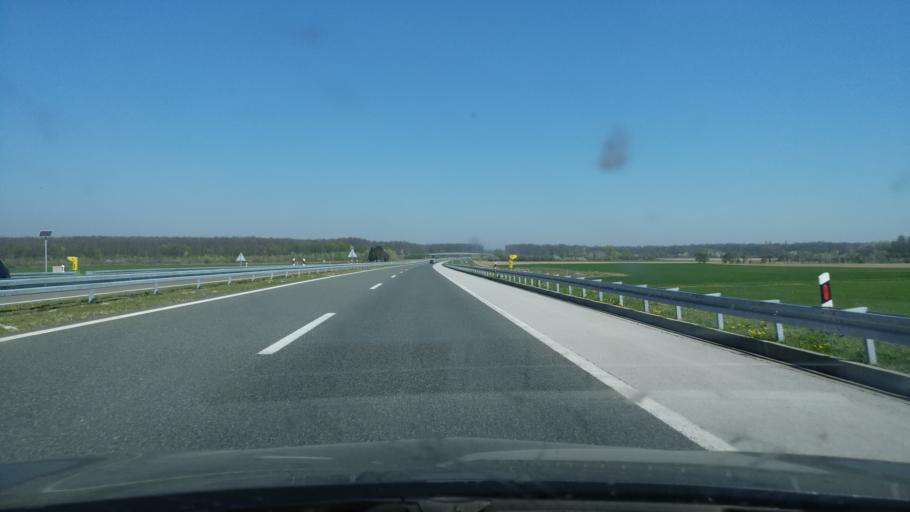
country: HR
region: Brodsko-Posavska
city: Vrpolje
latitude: 45.2279
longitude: 18.3306
